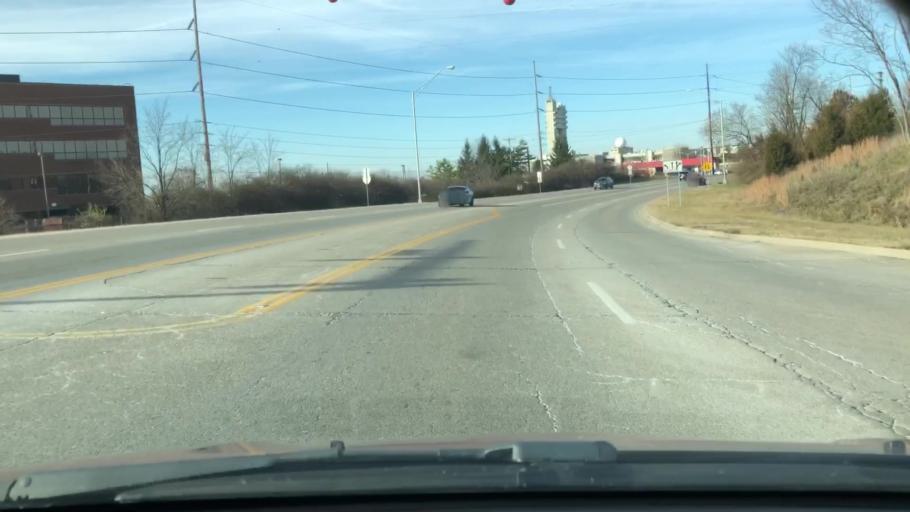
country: US
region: Ohio
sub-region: Greene County
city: Wright-Patterson AFB
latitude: 39.7728
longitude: -84.0791
